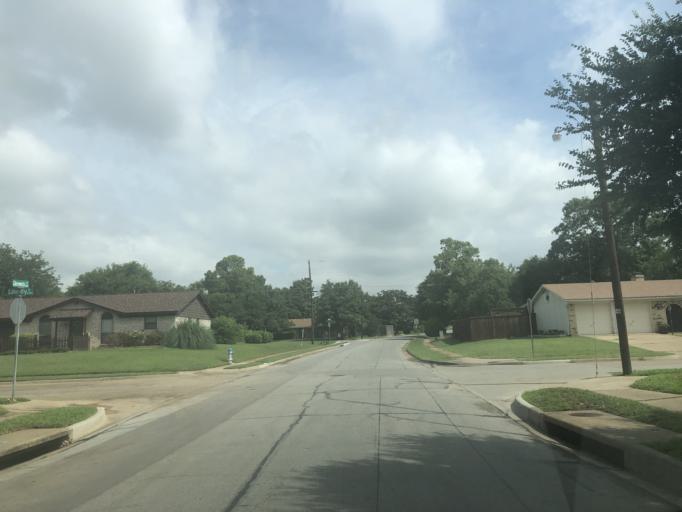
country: US
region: Texas
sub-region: Dallas County
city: Irving
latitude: 32.7950
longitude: -96.9737
